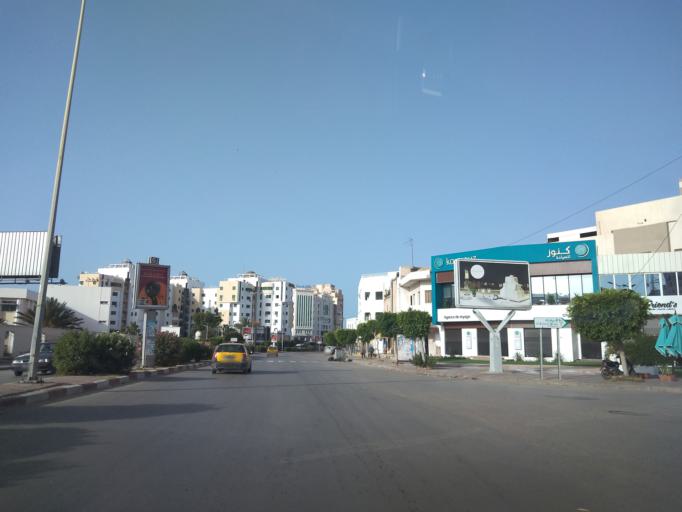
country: TN
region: Safaqis
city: Sfax
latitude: 34.7395
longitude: 10.7512
